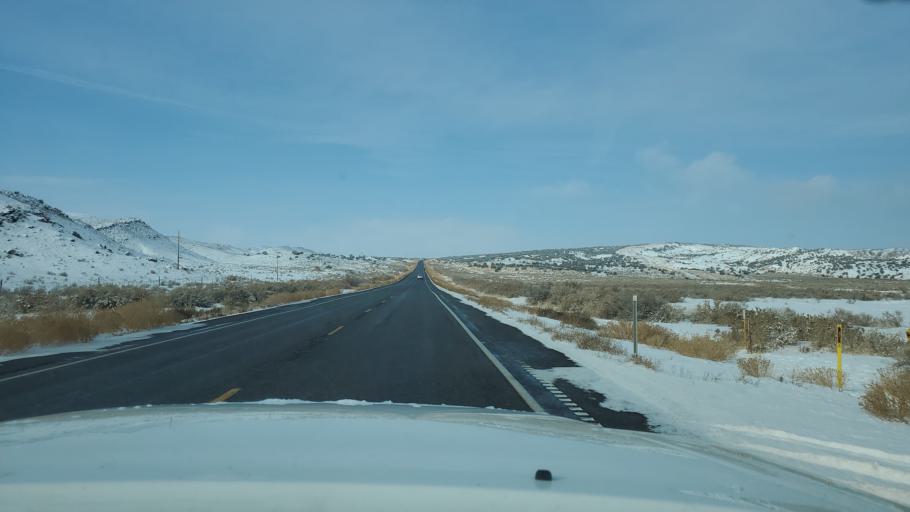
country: US
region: Utah
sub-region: Uintah County
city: Naples
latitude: 40.3173
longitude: -109.2375
